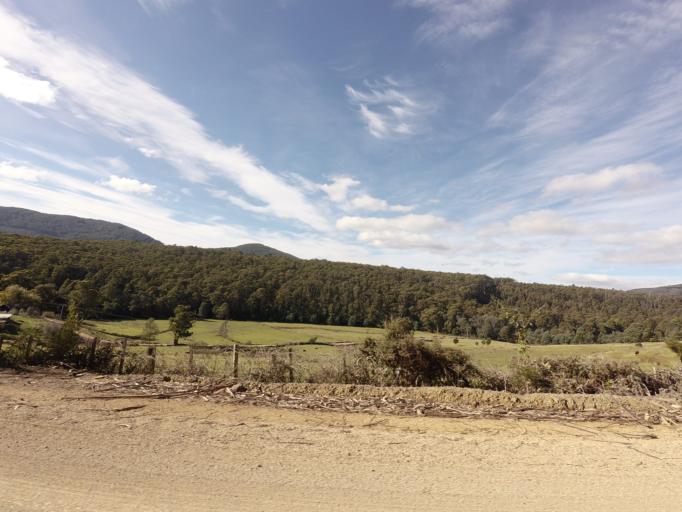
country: AU
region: Tasmania
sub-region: Clarence
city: Sandford
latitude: -43.1368
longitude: 147.7671
